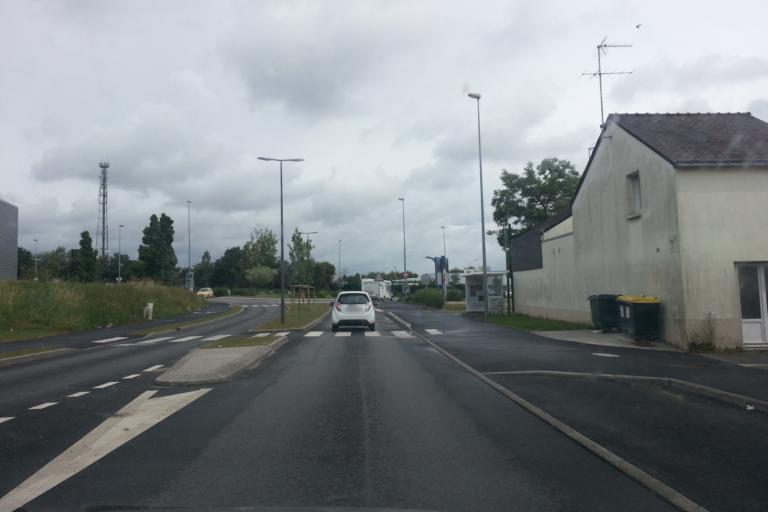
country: FR
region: Brittany
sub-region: Departement du Morbihan
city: Lanester
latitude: 47.7763
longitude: -3.3387
